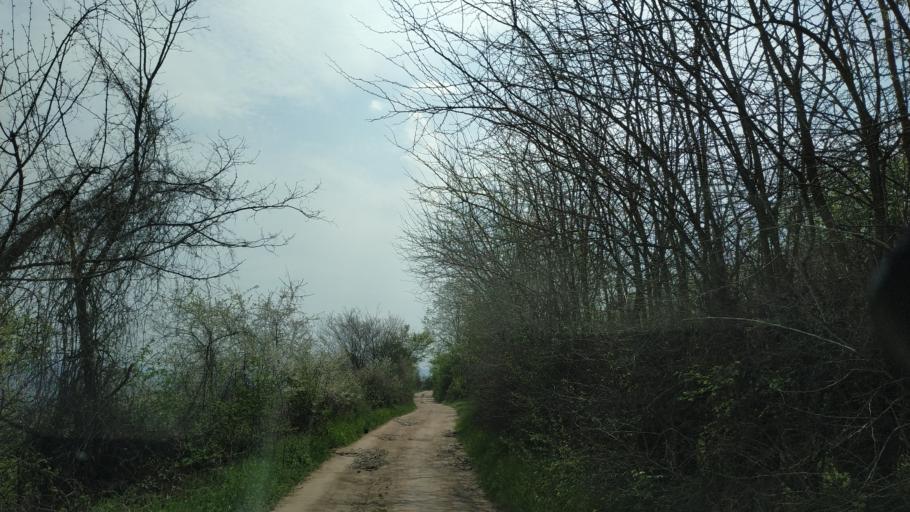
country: RS
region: Central Serbia
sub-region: Nisavski Okrug
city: Aleksinac
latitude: 43.5402
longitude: 21.7262
